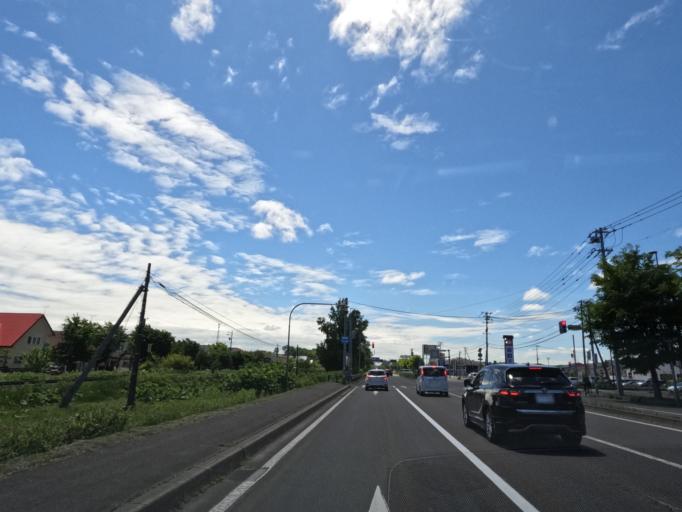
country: JP
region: Hokkaido
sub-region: Asahikawa-shi
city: Asahikawa
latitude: 43.7258
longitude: 142.3684
